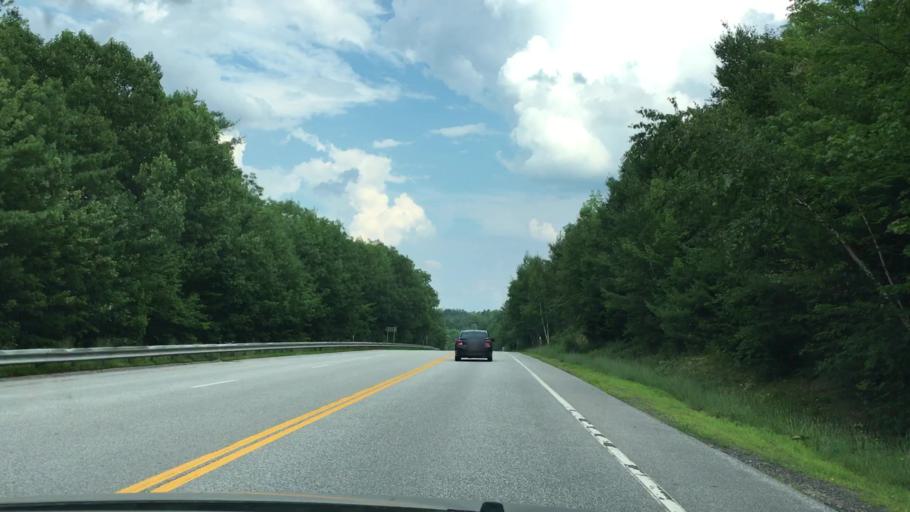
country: US
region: New Hampshire
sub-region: Belknap County
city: Gilford
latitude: 43.5743
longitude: -71.3625
